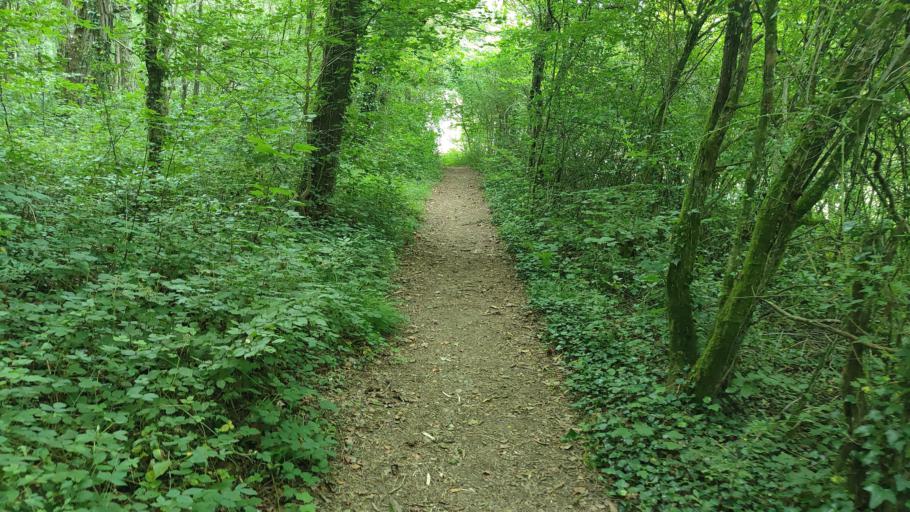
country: BE
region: Wallonia
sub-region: Province du Hainaut
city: Chimay
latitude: 50.0528
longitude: 4.3889
